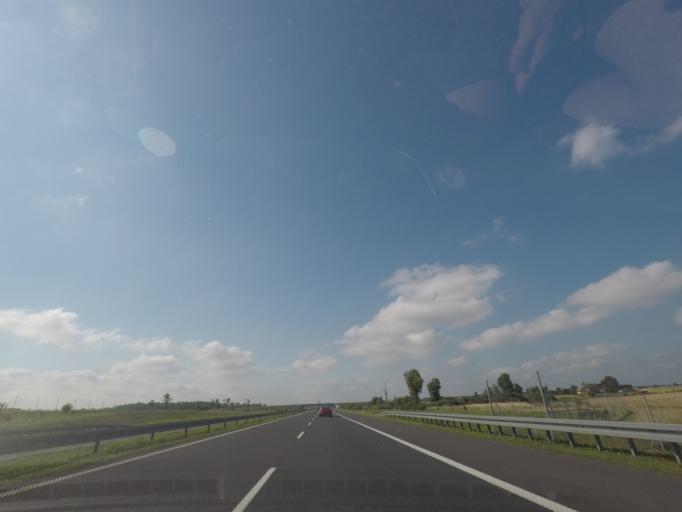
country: PL
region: Pomeranian Voivodeship
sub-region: Powiat starogardzki
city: Smetowo Graniczne
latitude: 53.7481
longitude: 18.6334
